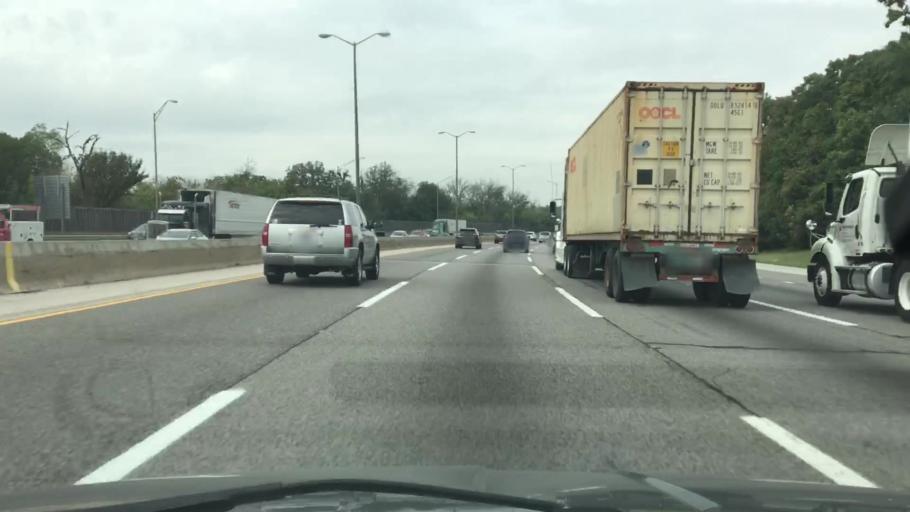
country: US
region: Illinois
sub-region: DuPage County
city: Oak Brook
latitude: 41.8249
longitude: -87.9175
